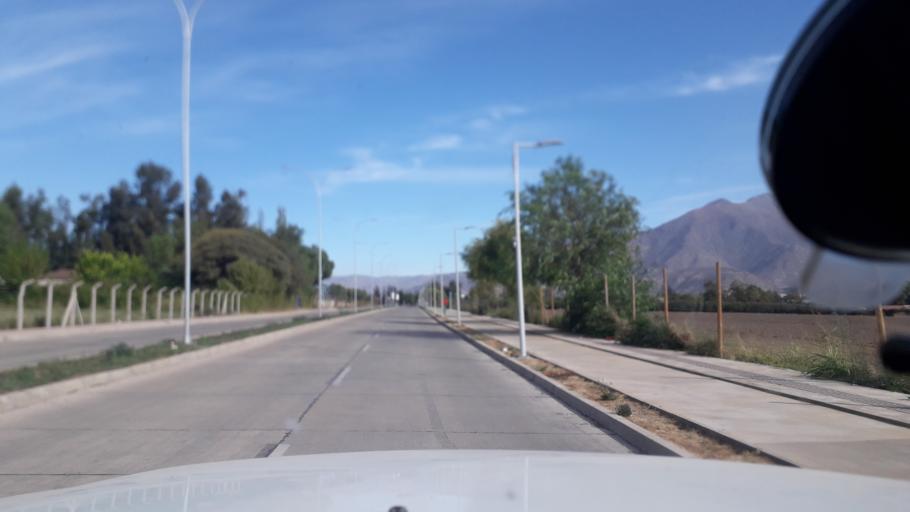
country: CL
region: Valparaiso
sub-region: Provincia de San Felipe
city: San Felipe
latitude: -32.7467
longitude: -70.7107
